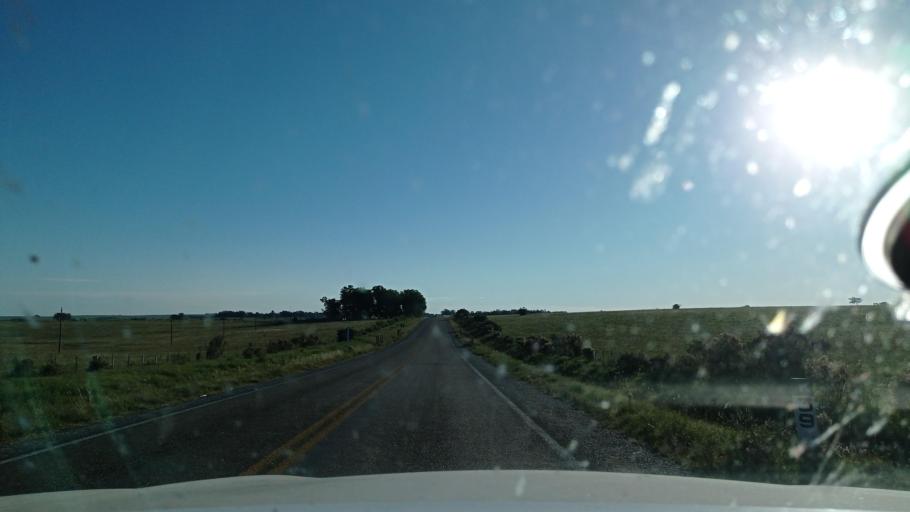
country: UY
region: Florida
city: Casupa
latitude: -34.0066
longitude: -55.8053
